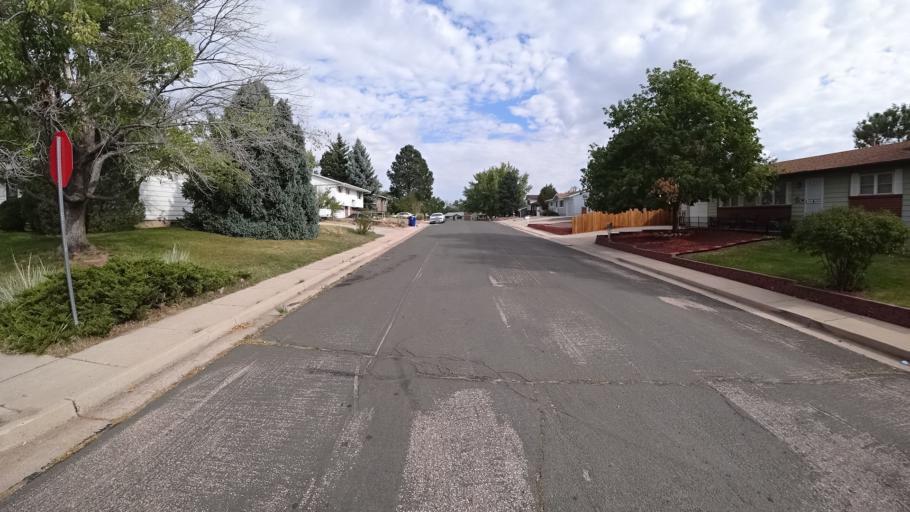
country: US
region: Colorado
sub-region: El Paso County
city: Cimarron Hills
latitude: 38.8436
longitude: -104.7487
